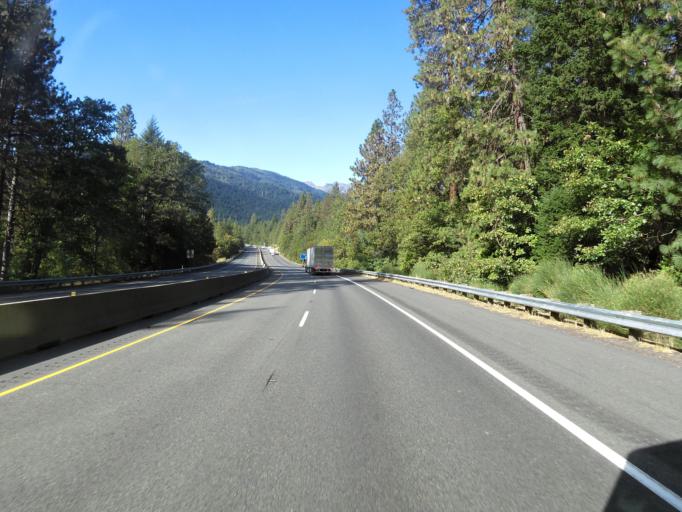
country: US
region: California
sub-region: Siskiyou County
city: Dunsmuir
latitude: 41.1517
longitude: -122.3074
